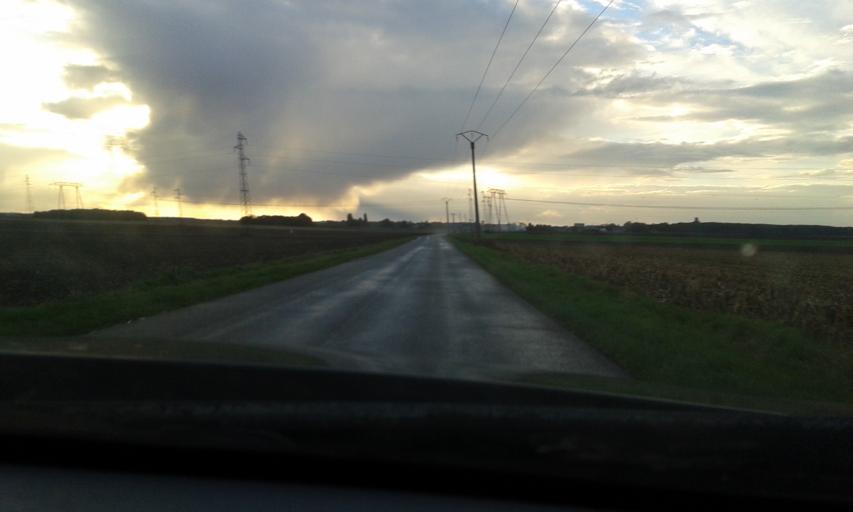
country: FR
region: Centre
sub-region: Departement du Loiret
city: Gidy
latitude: 47.9897
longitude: 1.8264
